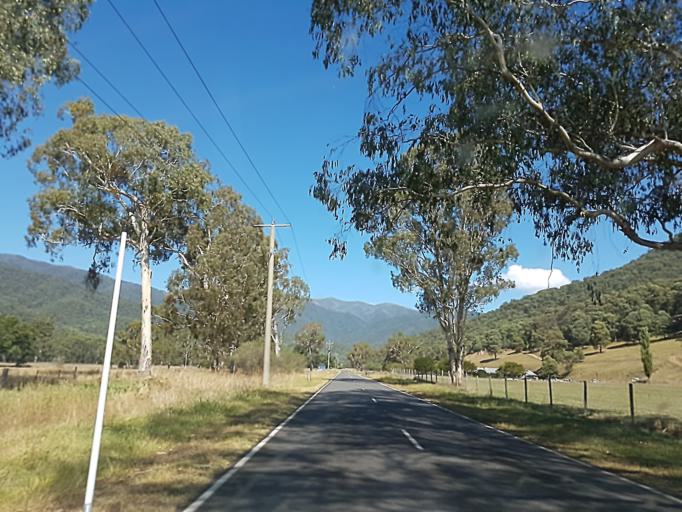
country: AU
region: Victoria
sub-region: Alpine
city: Mount Beauty
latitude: -36.8260
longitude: 147.0694
